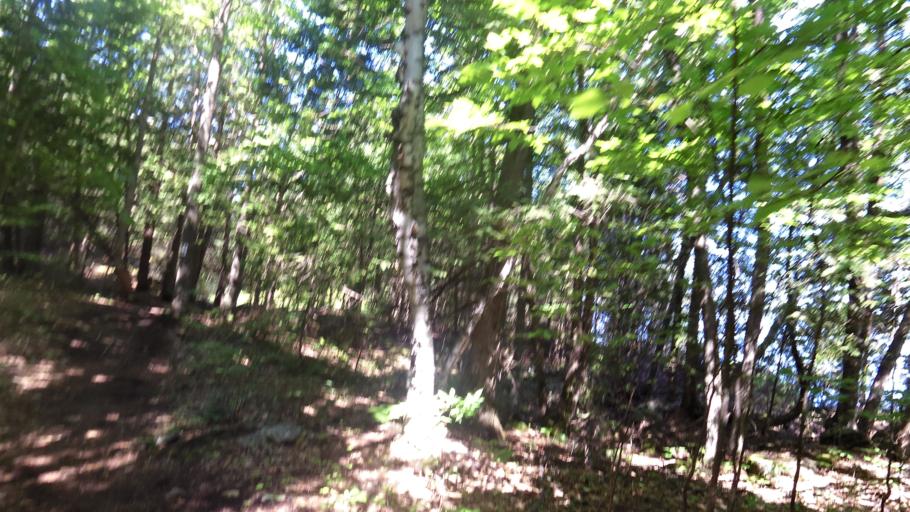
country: CA
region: Ontario
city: Arnprior
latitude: 45.4641
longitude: -76.2637
